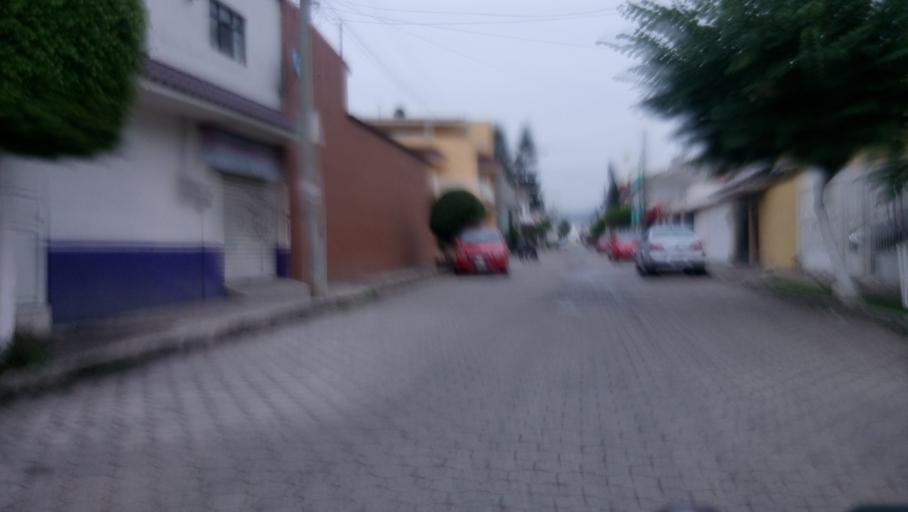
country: MX
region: Guanajuato
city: Leon
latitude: 21.1469
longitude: -101.6622
